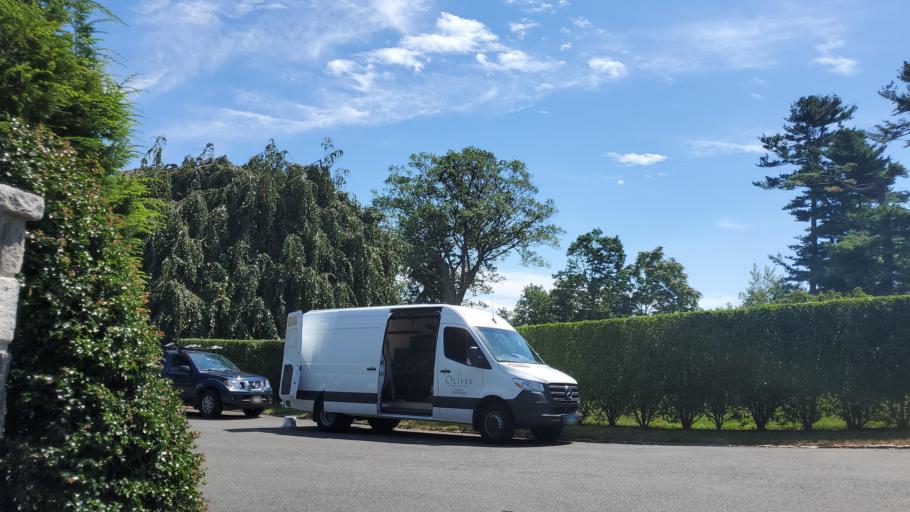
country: US
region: Connecticut
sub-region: Fairfield County
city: Westport
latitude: 41.1125
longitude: -73.3478
